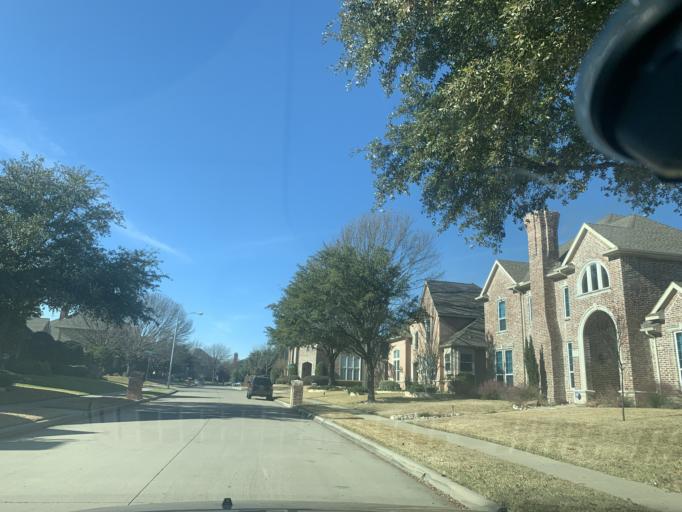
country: US
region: Texas
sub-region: Denton County
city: The Colony
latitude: 33.0536
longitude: -96.8189
